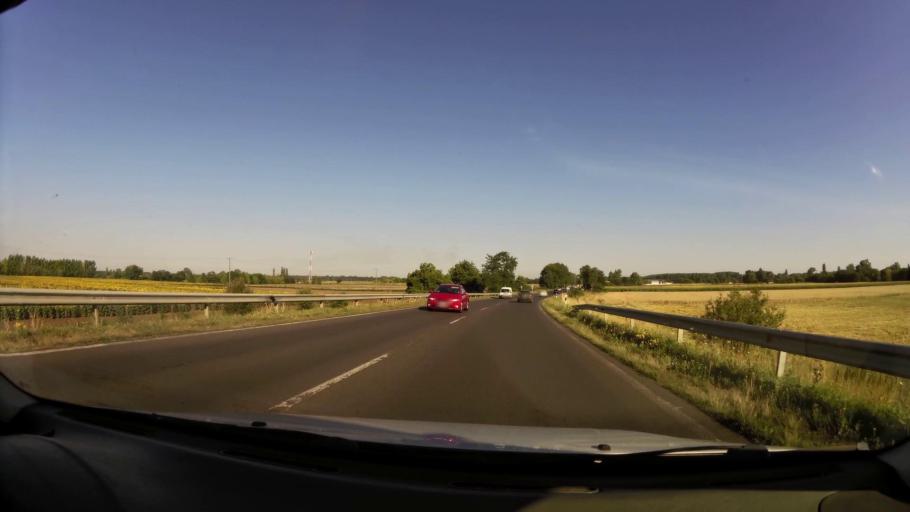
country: HU
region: Pest
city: Monor
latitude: 47.3166
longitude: 19.4818
